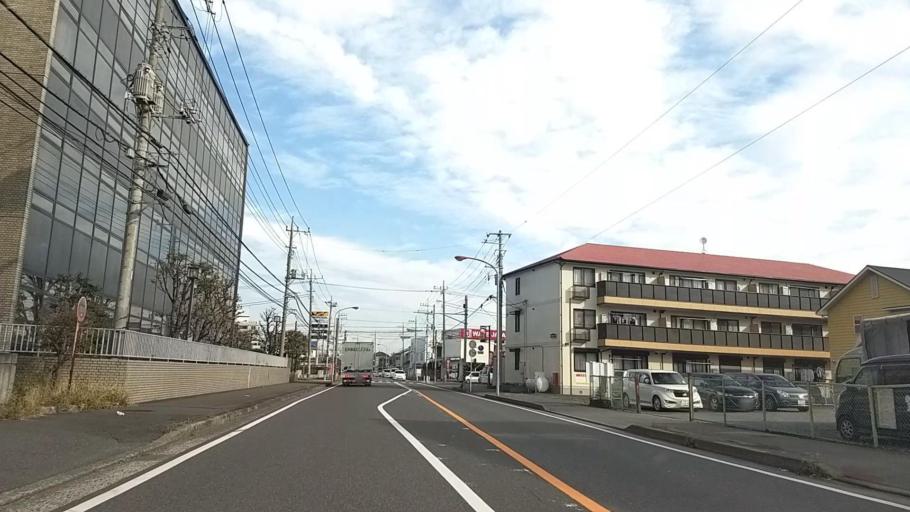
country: JP
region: Kanagawa
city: Atsugi
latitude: 35.4175
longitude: 139.3642
